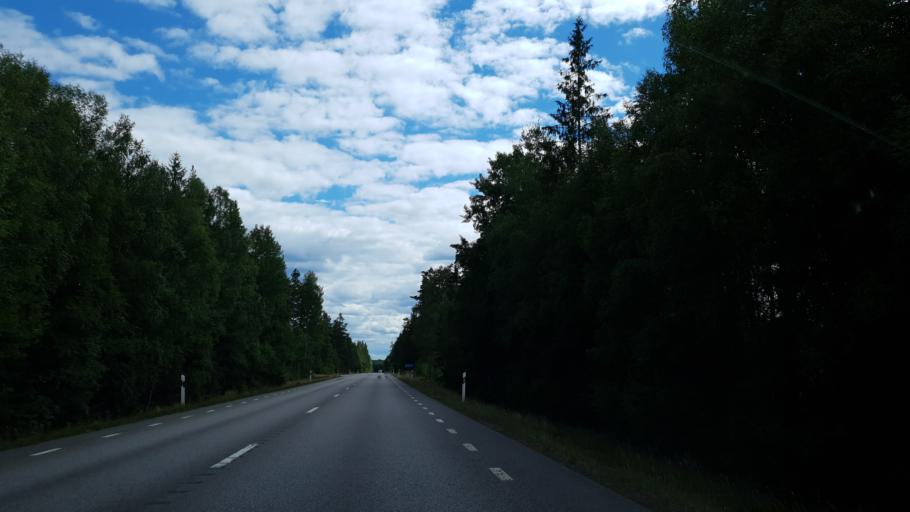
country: SE
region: Kronoberg
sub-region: Uppvidinge Kommun
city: Lenhovda
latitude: 56.8908
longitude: 15.3727
